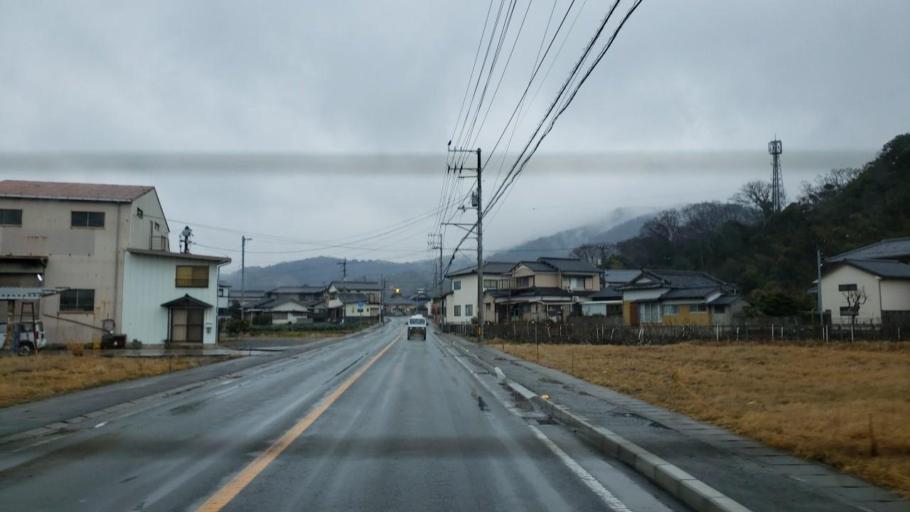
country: JP
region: Tokushima
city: Narutocho-mitsuishi
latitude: 34.1622
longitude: 134.5451
